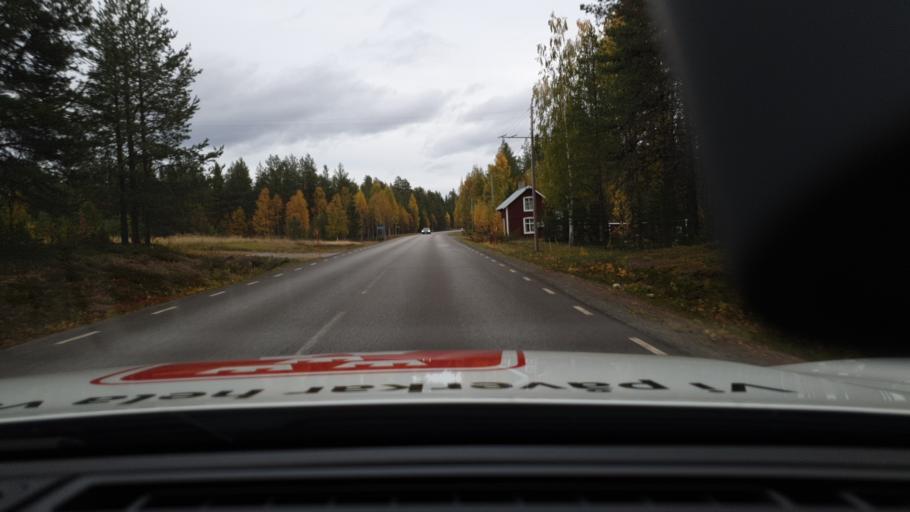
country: SE
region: Vaesterbotten
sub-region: Norsjo Kommun
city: Norsjoe
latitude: 65.4098
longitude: 19.7560
